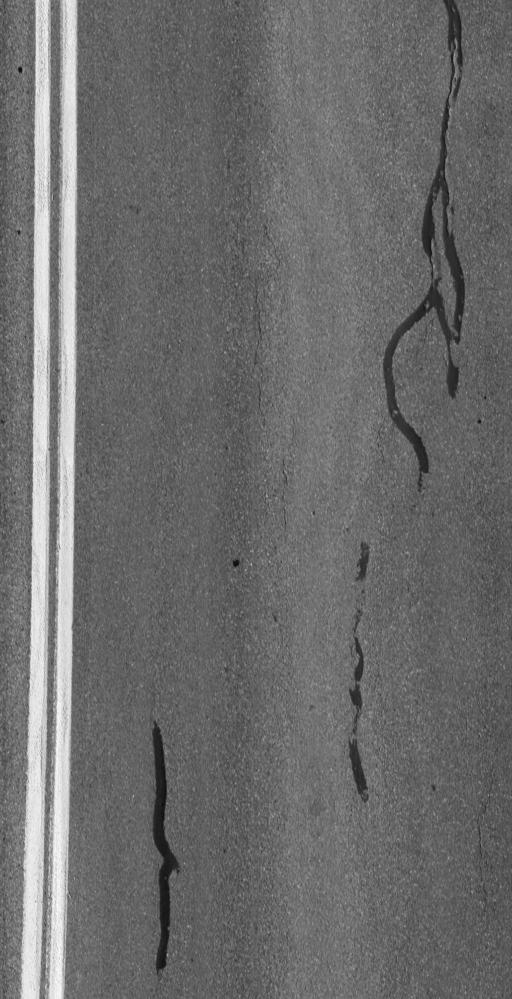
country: US
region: Vermont
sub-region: Chittenden County
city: Burlington
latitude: 44.4625
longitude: -73.2016
